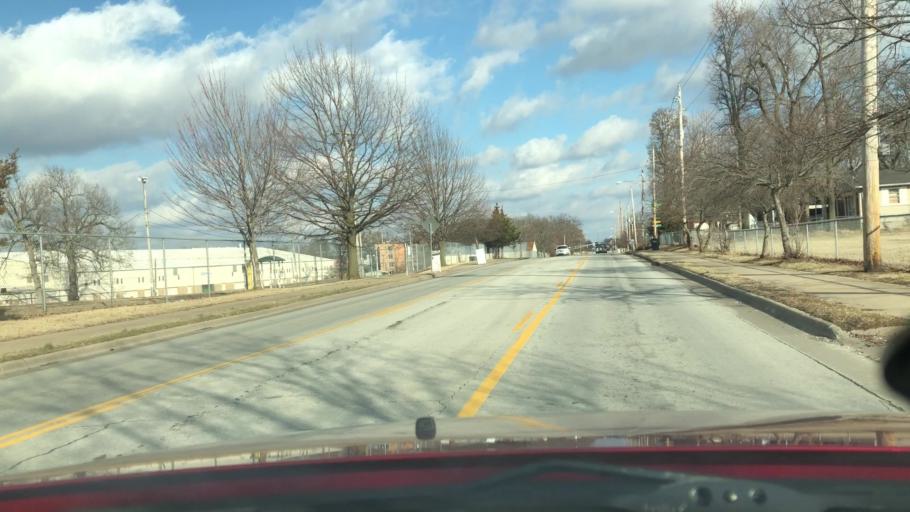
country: US
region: Missouri
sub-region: Greene County
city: Springfield
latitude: 37.2517
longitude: -93.3005
